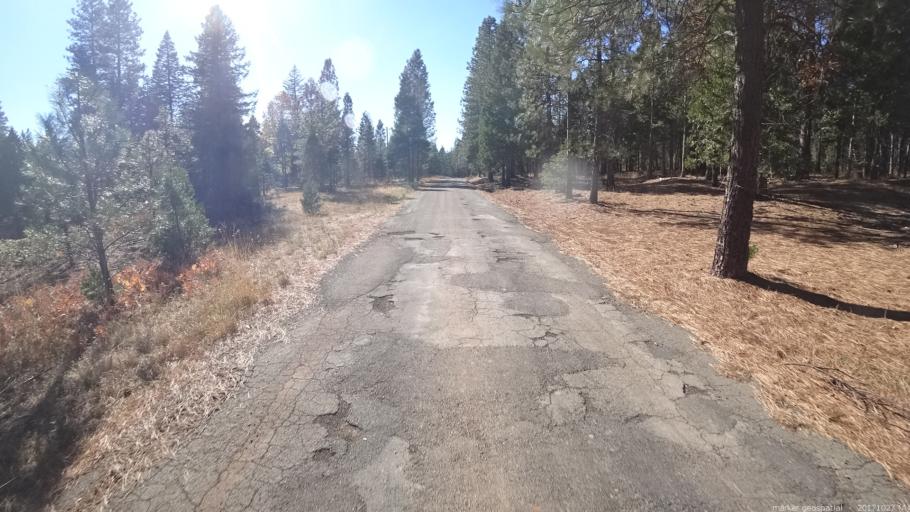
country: US
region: California
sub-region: Shasta County
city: Shingletown
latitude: 40.6140
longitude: -121.8198
